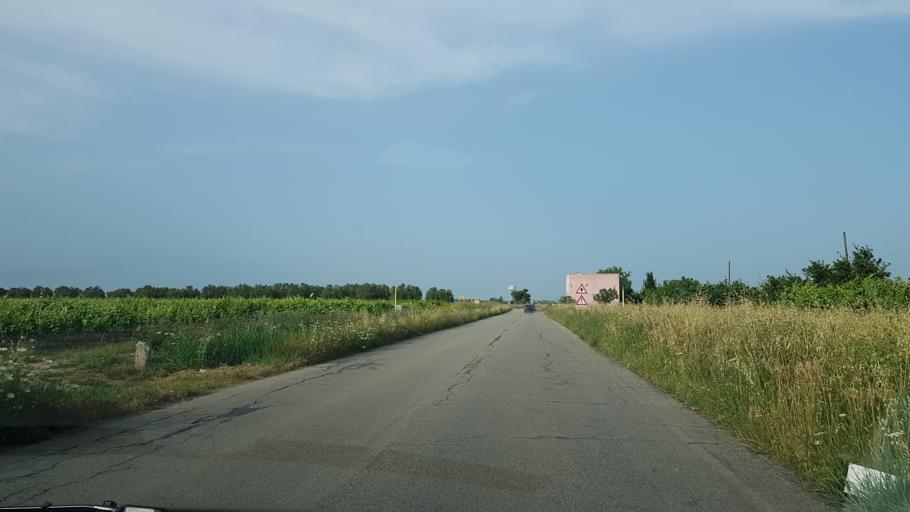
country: IT
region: Apulia
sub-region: Provincia di Brindisi
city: San Pancrazio Salentino
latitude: 40.4264
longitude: 17.8632
